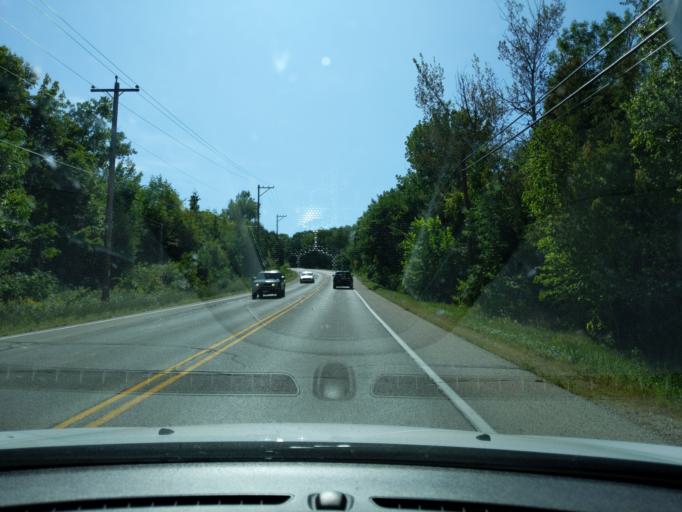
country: US
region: Michigan
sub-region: Delta County
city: Escanaba
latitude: 45.2499
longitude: -87.0808
